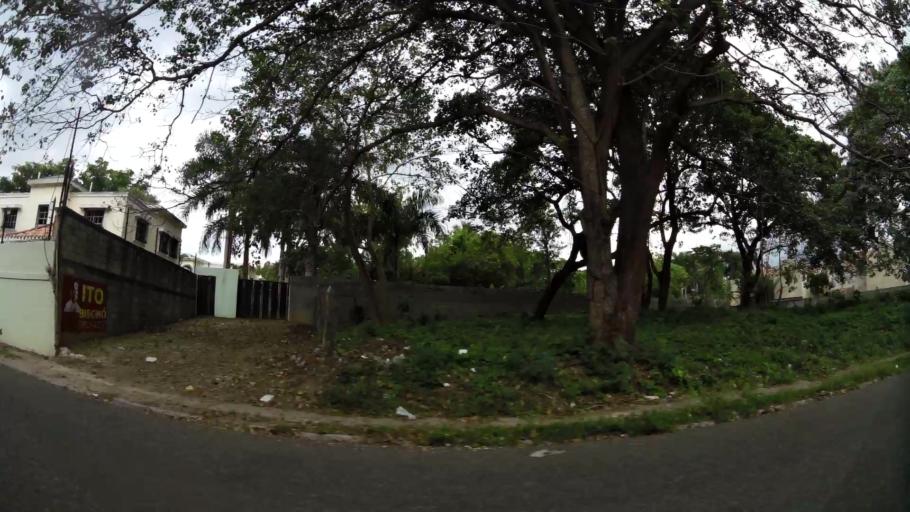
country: DO
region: Nacional
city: La Agustina
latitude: 18.5087
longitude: -69.9459
